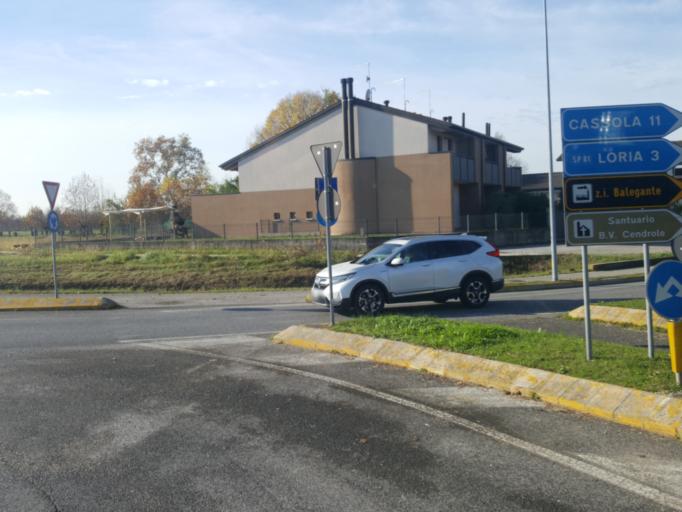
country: IT
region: Veneto
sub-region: Provincia di Treviso
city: Riese Pio X
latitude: 45.7304
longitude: 11.9054
